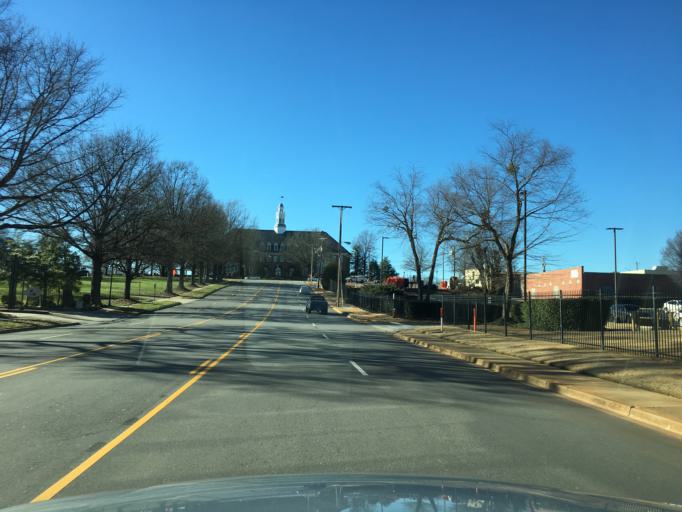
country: US
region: South Carolina
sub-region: Greenville County
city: Greenville
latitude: 34.8510
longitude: -82.4035
